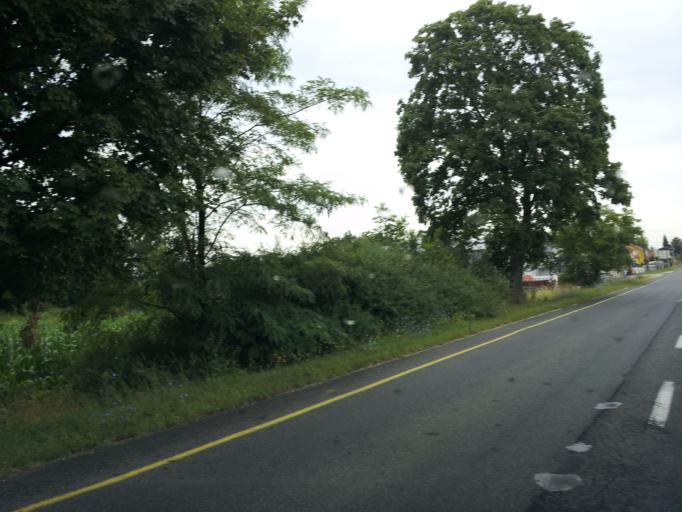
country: HU
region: Vas
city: Kormend
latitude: 46.9622
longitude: 16.6042
